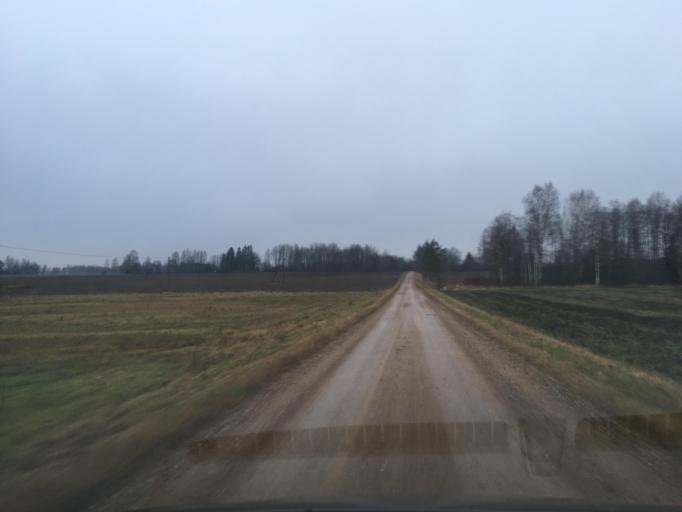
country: EE
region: Tartu
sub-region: Alatskivi vald
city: Kallaste
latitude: 58.3902
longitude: 27.0250
